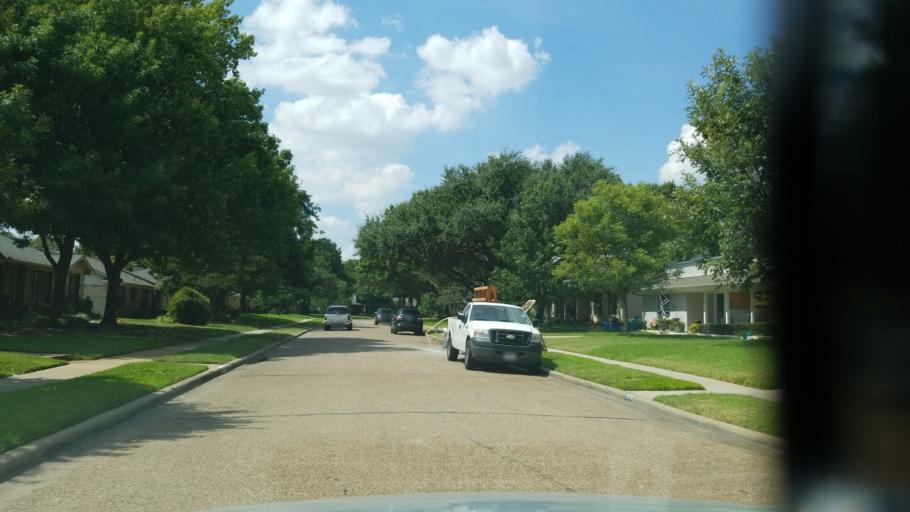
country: US
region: Texas
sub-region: Dallas County
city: Richardson
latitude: 32.9654
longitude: -96.7643
